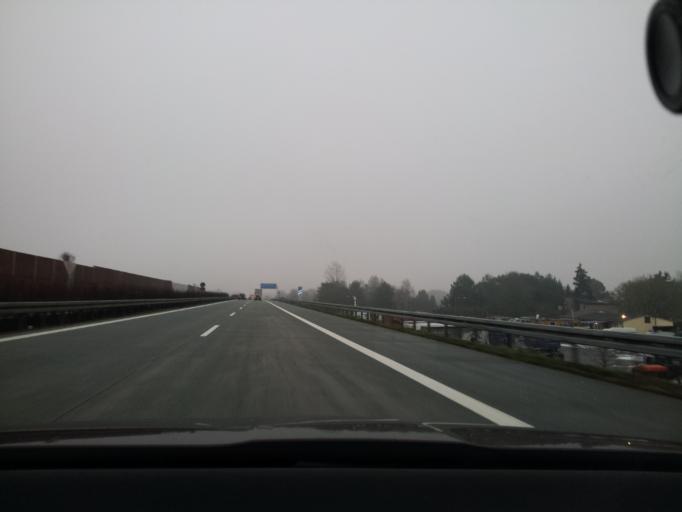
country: DE
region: Brandenburg
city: Furstenwalde
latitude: 52.3347
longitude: 14.0700
